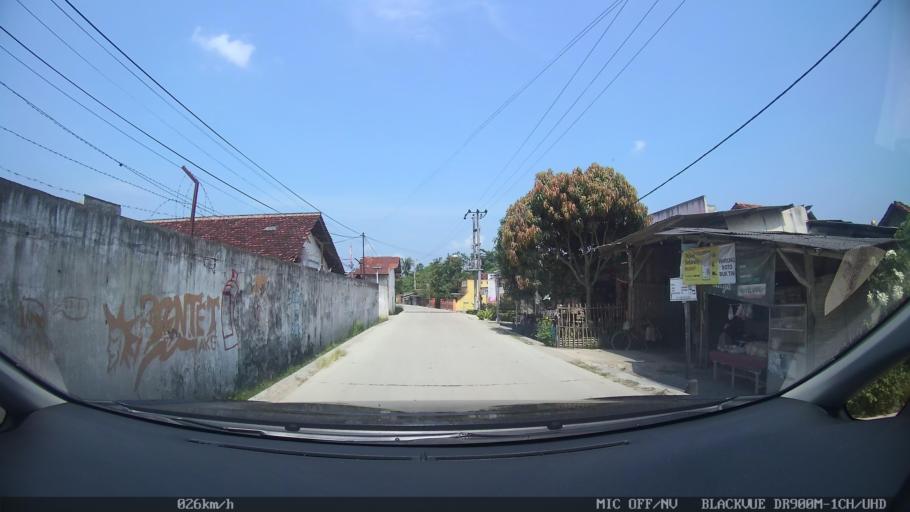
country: ID
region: Lampung
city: Natar
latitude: -5.2663
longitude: 105.1881
